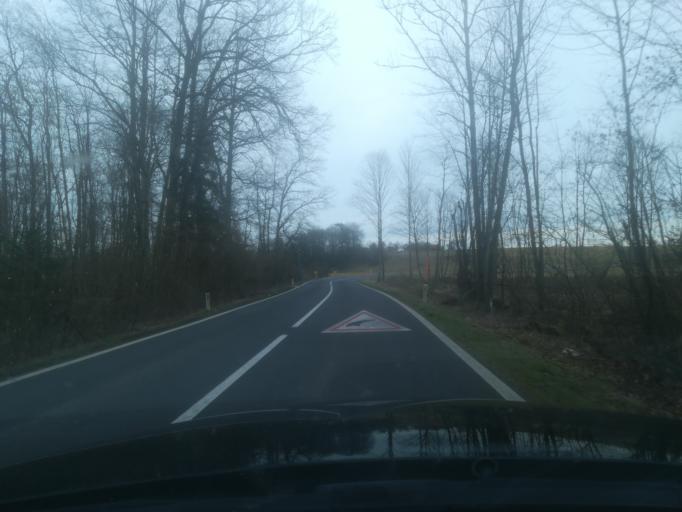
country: AT
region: Upper Austria
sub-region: Wels-Land
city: Bad Wimsbach-Neydharting
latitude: 48.0740
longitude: 13.8887
